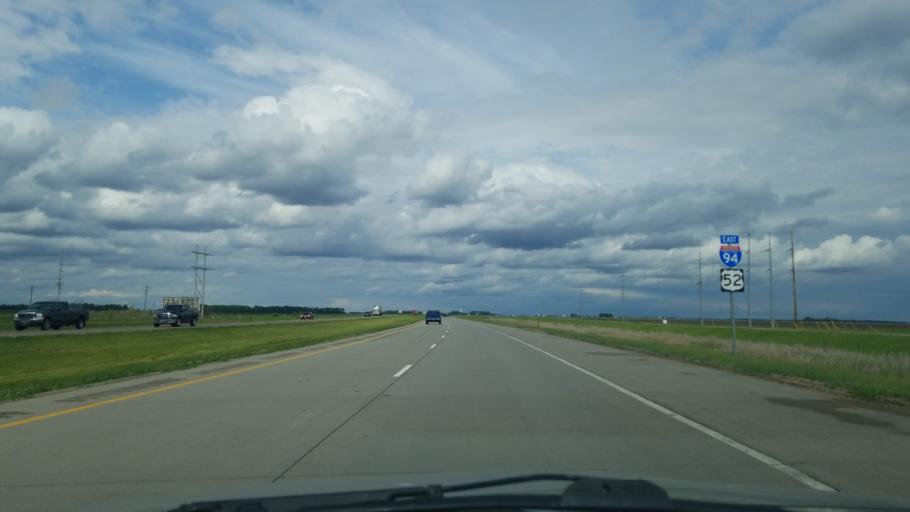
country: US
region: North Dakota
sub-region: Cass County
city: Casselton
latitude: 46.8745
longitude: -97.2028
